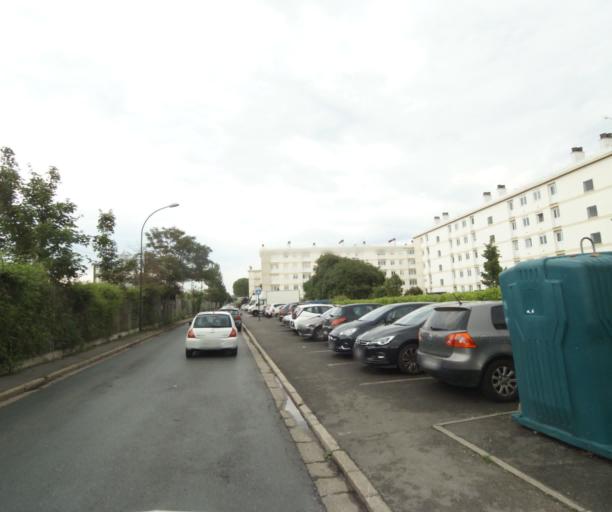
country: FR
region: Ile-de-France
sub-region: Departement du Val-d'Oise
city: Argenteuil
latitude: 48.9485
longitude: 2.2249
